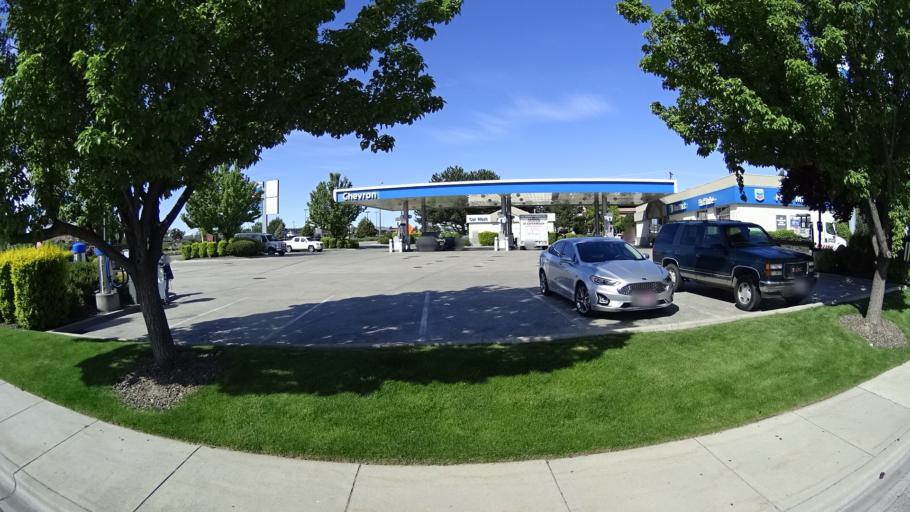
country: US
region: Idaho
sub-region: Ada County
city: Boise
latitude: 43.5701
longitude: -116.2171
